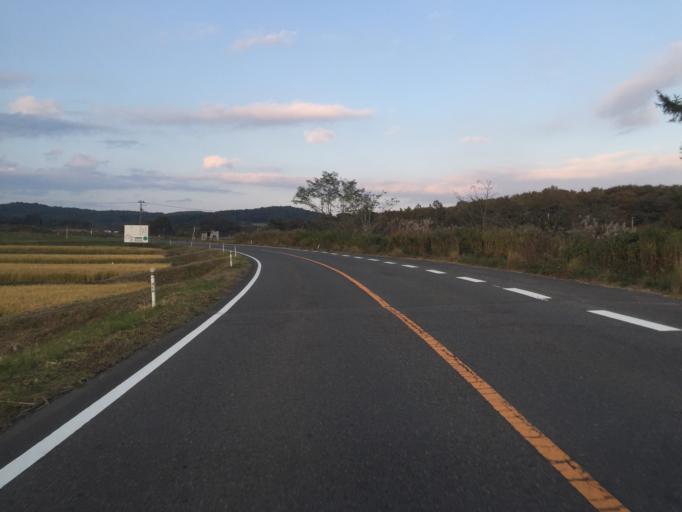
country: JP
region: Fukushima
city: Nihommatsu
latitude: 37.5892
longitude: 140.3545
